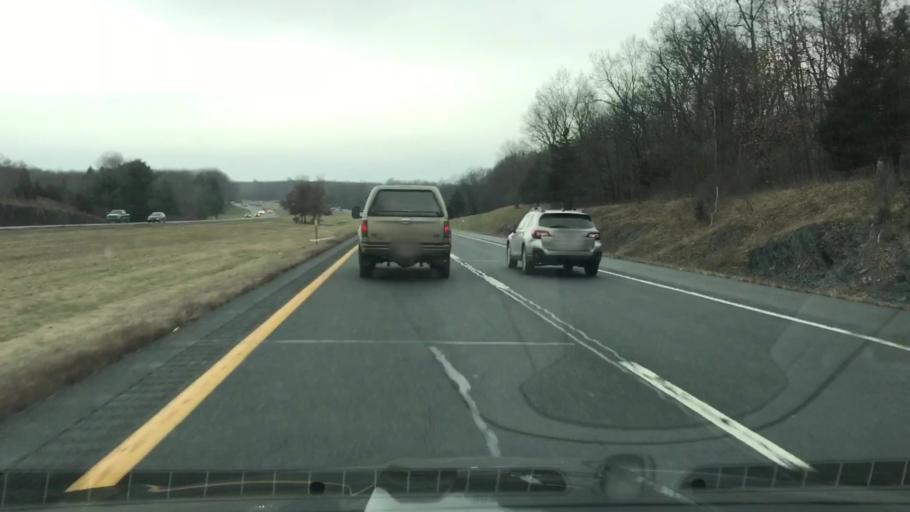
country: US
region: New York
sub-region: Orange County
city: Walden
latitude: 41.5152
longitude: -74.1610
